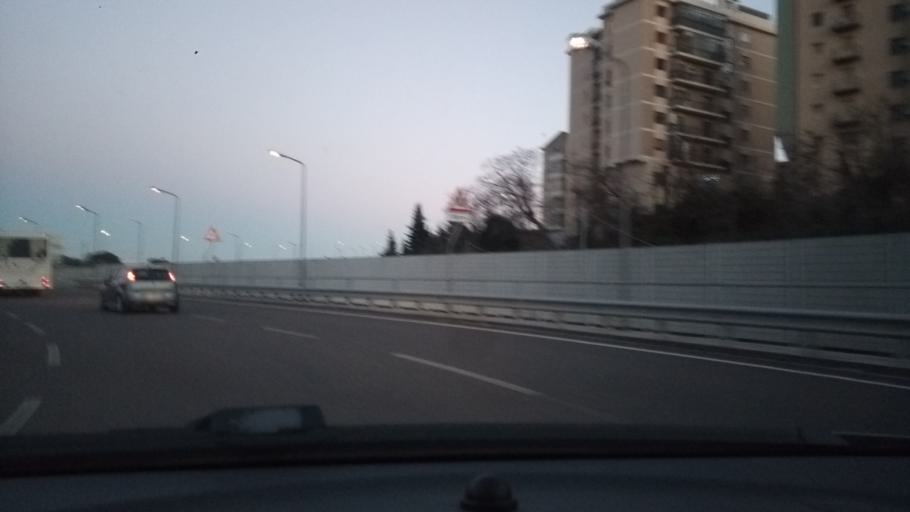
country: IT
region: Calabria
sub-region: Provincia di Catanzaro
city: Siano
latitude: 38.9113
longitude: 16.5911
